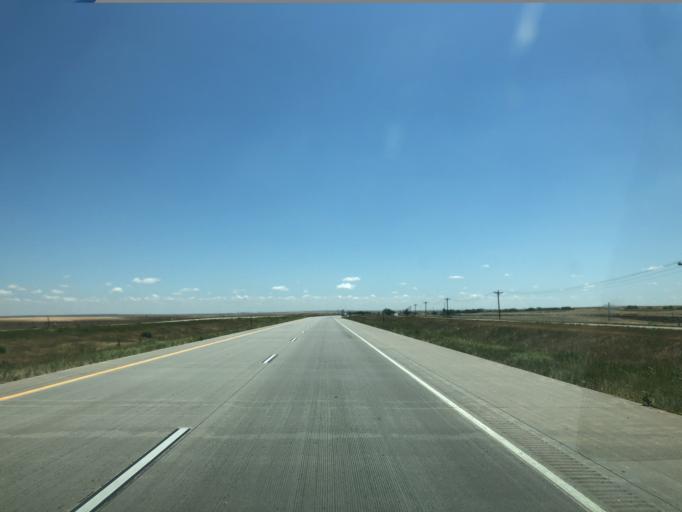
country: US
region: Colorado
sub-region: Arapahoe County
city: Byers
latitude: 39.6990
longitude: -104.1644
